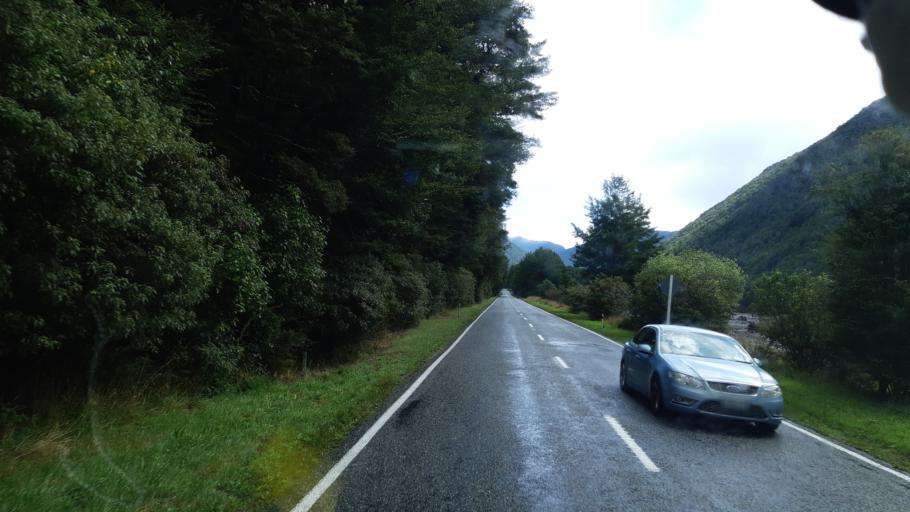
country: NZ
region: Canterbury
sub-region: Hurunui District
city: Amberley
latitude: -42.3807
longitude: 172.3225
